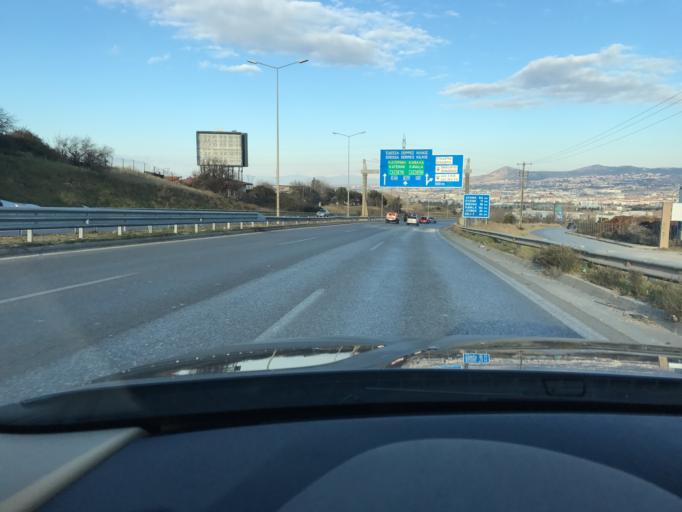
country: GR
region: Central Macedonia
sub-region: Nomos Thessalonikis
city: Polichni
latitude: 40.6648
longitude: 22.9651
